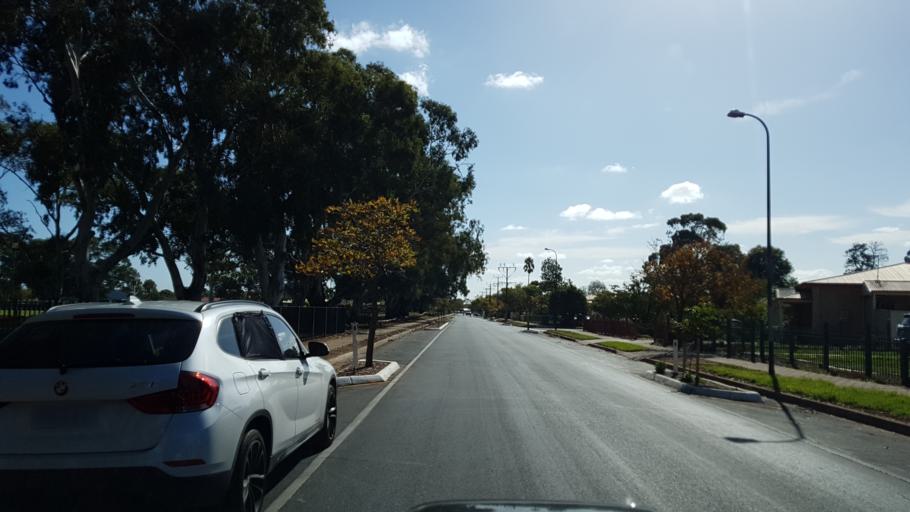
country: AU
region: South Australia
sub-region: Salisbury
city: Salisbury
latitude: -34.7520
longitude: 138.6343
